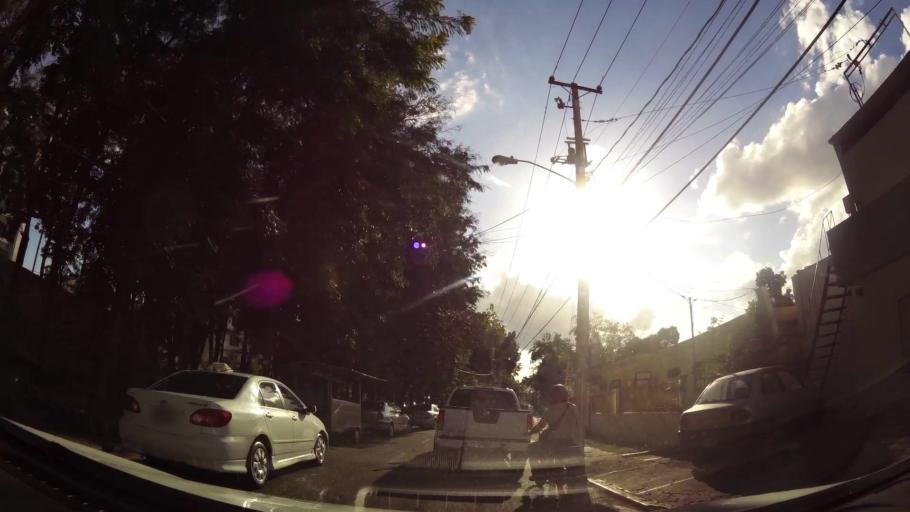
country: DO
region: Santiago
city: Santiago de los Caballeros
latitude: 19.4635
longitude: -70.6927
